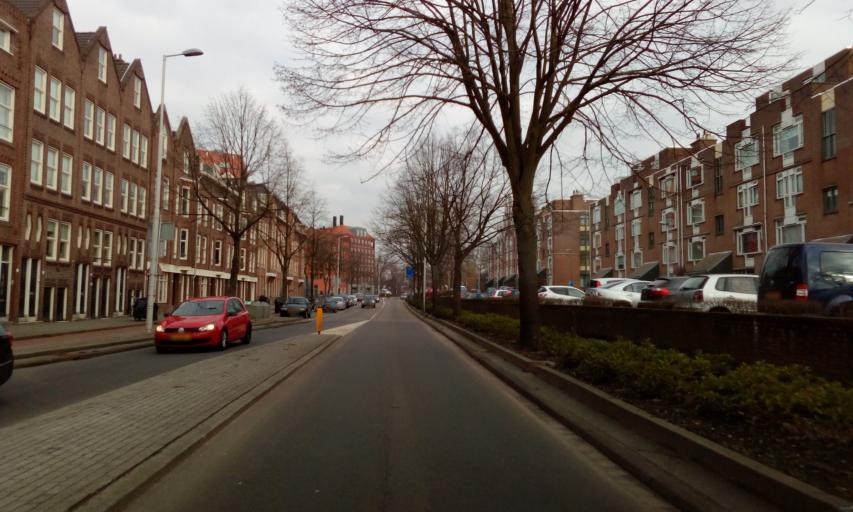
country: NL
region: South Holland
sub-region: Gemeente Rotterdam
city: Rotterdam
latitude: 51.9343
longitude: 4.4981
